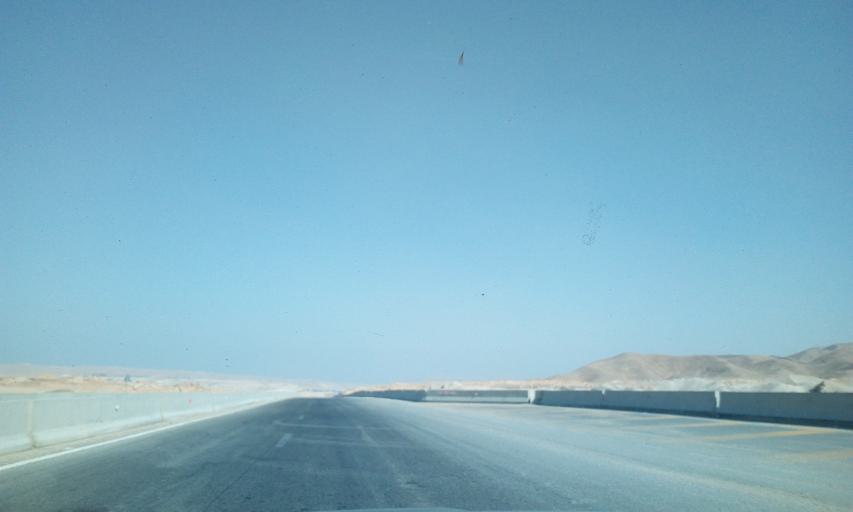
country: EG
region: As Suways
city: Ain Sukhna
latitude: 29.4449
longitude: 32.3537
